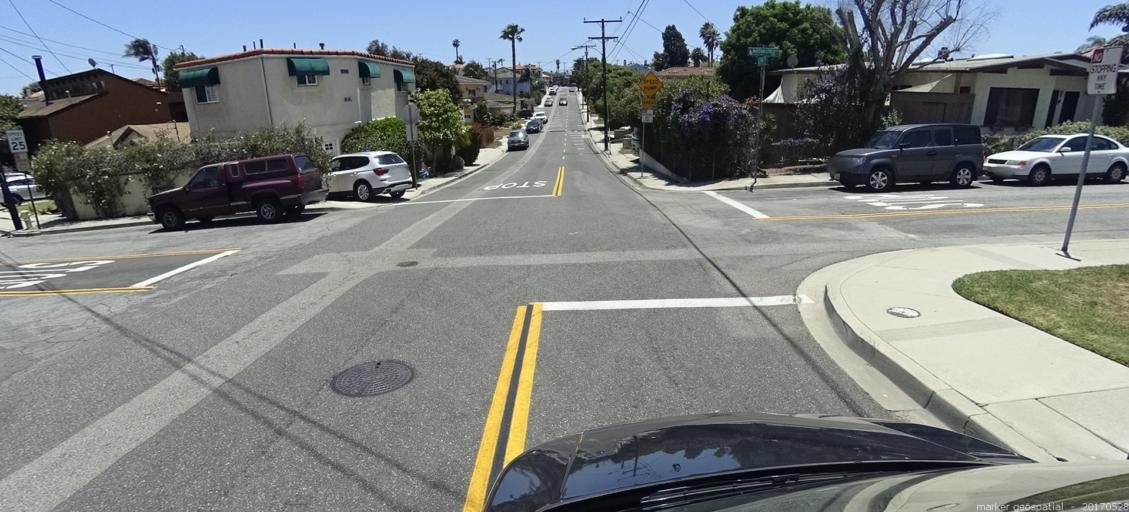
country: US
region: California
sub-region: Los Angeles County
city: Hermosa Beach
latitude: 33.8652
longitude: -118.3829
